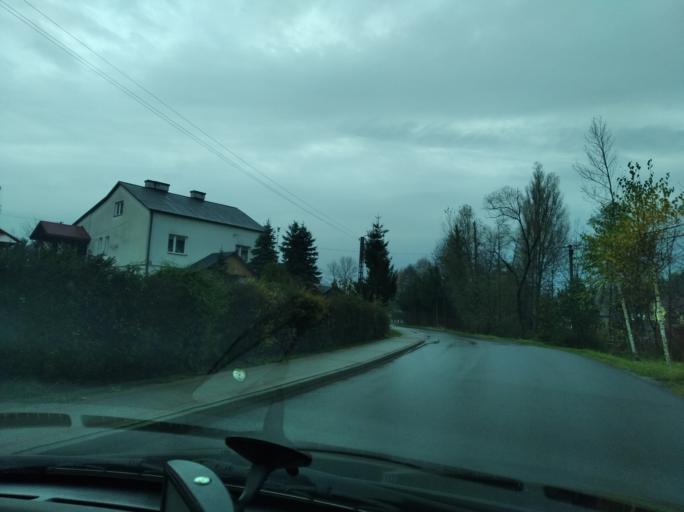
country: PL
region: Subcarpathian Voivodeship
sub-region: Powiat rzeszowski
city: Lubenia
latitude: 49.9245
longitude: 21.9463
